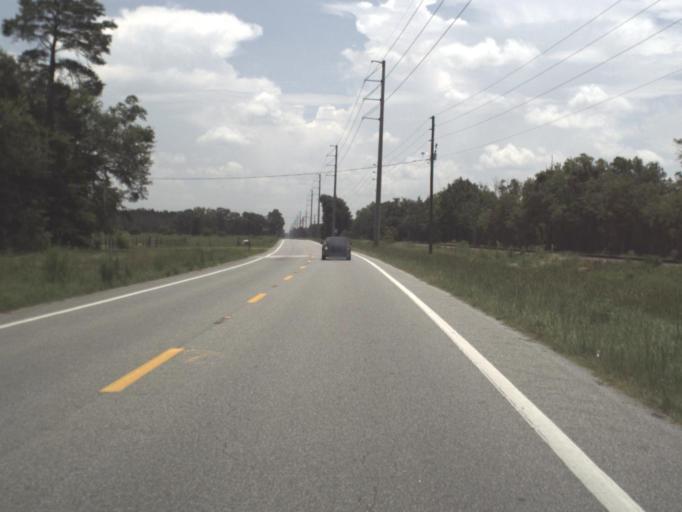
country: US
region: Florida
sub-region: Madison County
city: Madison
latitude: 30.4168
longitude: -83.2908
